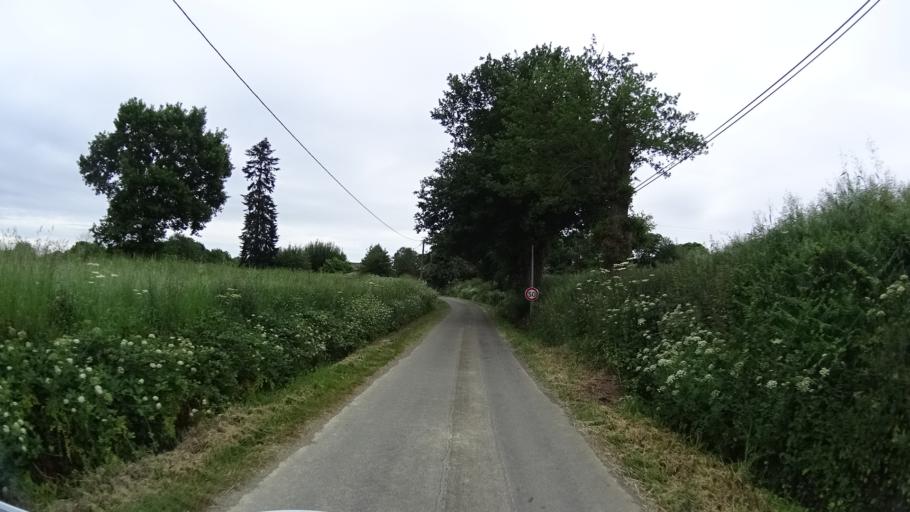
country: FR
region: Brittany
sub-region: Departement d'Ille-et-Vilaine
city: Orgeres
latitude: 47.9808
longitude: -1.6514
